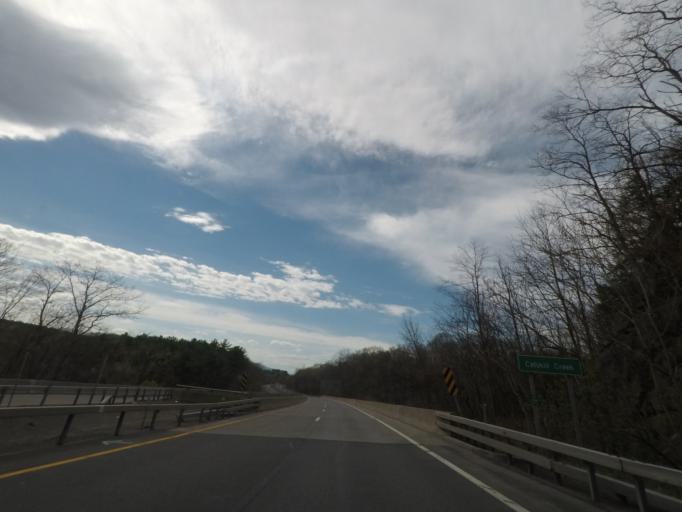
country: US
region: New York
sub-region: Greene County
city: Jefferson Heights
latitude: 42.2483
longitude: -73.8958
